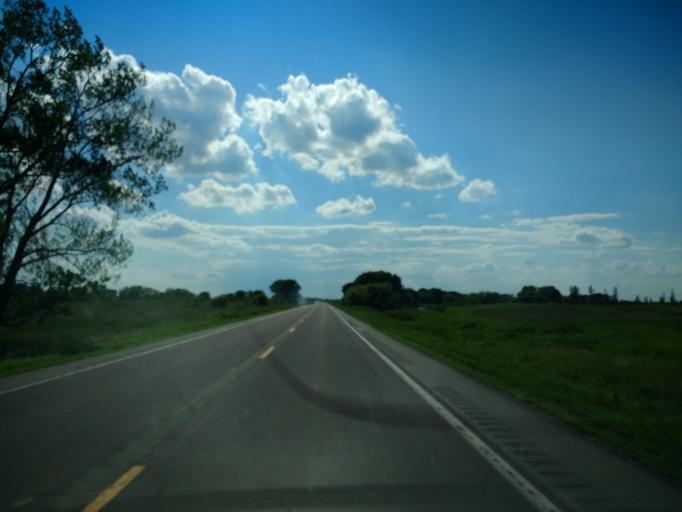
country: US
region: Iowa
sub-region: Clay County
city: Spencer
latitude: 43.1841
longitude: -95.1840
